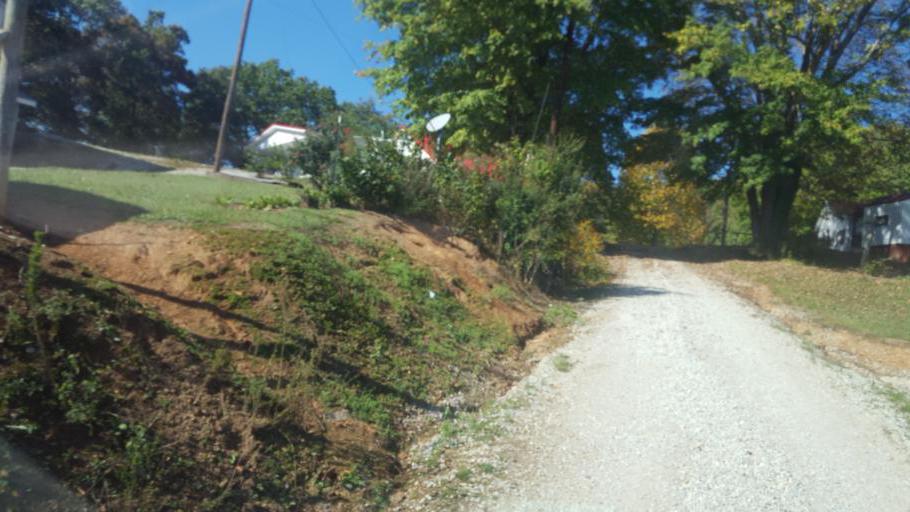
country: US
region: Kentucky
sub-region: Fleming County
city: Flemingsburg
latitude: 38.4657
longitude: -83.5727
